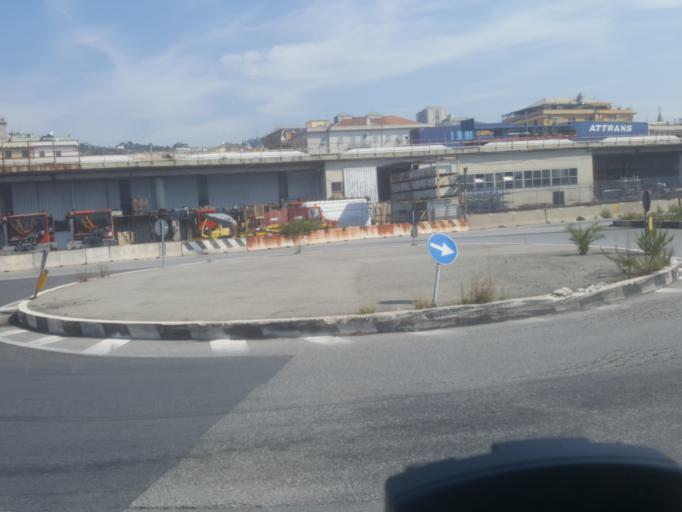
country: IT
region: Liguria
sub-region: Provincia di Genova
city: San Teodoro
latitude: 44.4078
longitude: 8.8911
